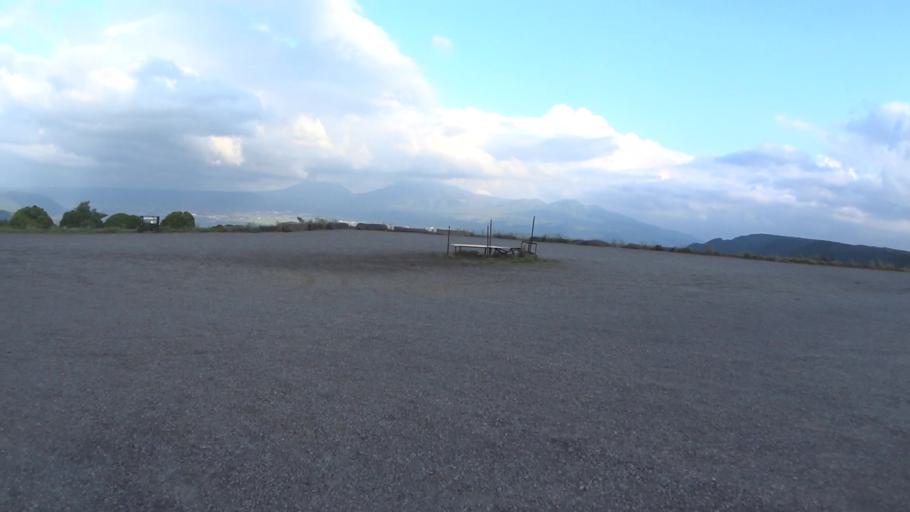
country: JP
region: Kumamoto
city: Aso
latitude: 33.0001
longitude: 131.0181
